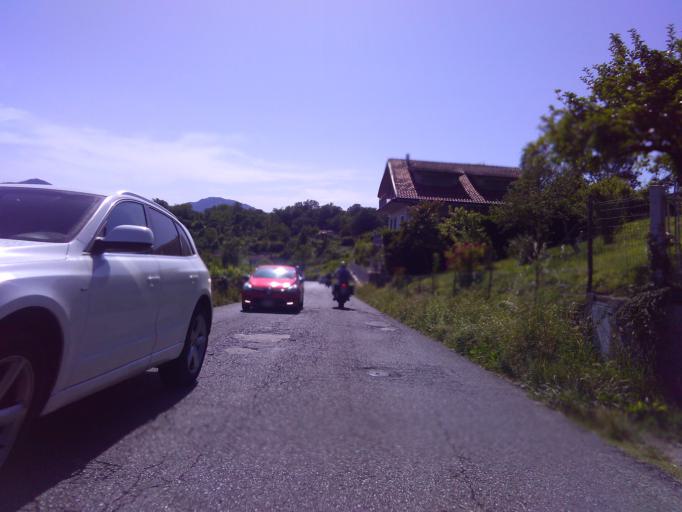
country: IT
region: Tuscany
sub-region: Provincia di Massa-Carrara
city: Monti
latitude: 44.2440
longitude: 10.0068
